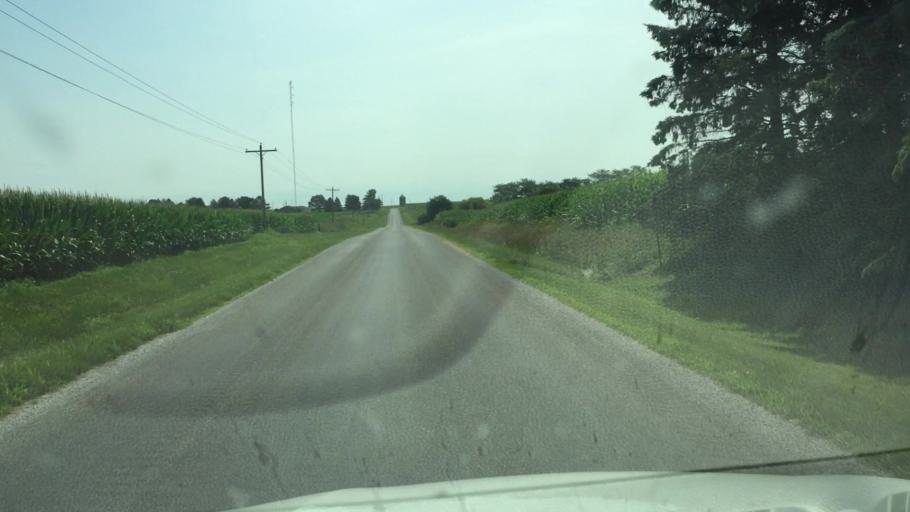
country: US
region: Illinois
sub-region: Hancock County
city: Nauvoo
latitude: 40.5112
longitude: -91.3362
